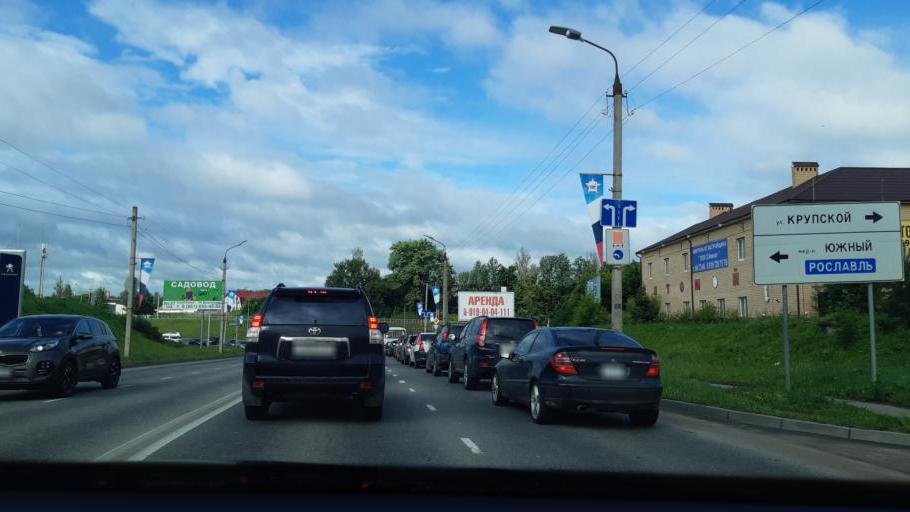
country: RU
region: Smolensk
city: Smolensk
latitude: 54.7572
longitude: 32.0739
